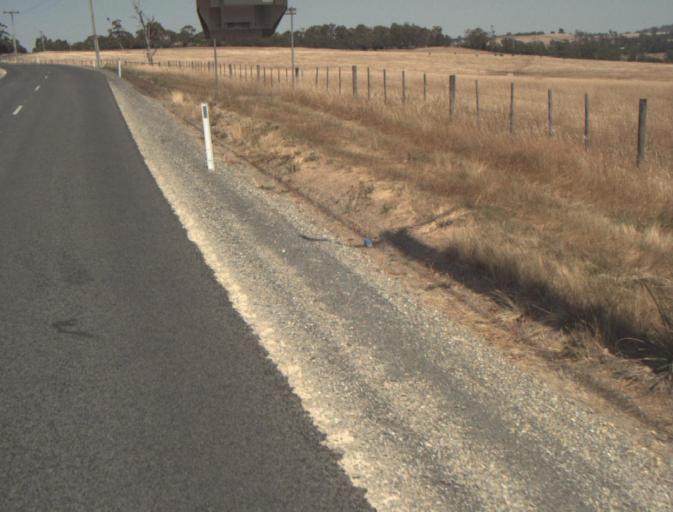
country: AU
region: Tasmania
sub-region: Launceston
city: Newstead
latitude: -41.4812
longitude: 147.1911
